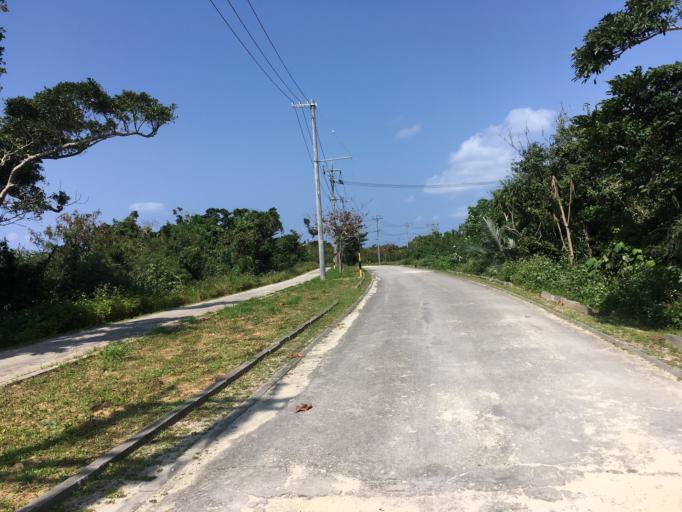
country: JP
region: Okinawa
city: Ishigaki
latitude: 24.3268
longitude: 124.0796
